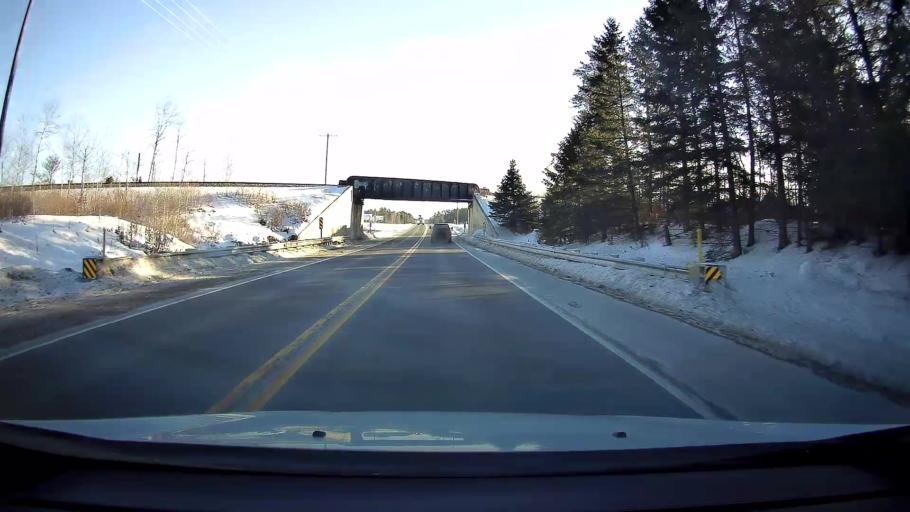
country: US
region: Wisconsin
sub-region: Sawyer County
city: Hayward
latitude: 45.9975
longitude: -91.6168
